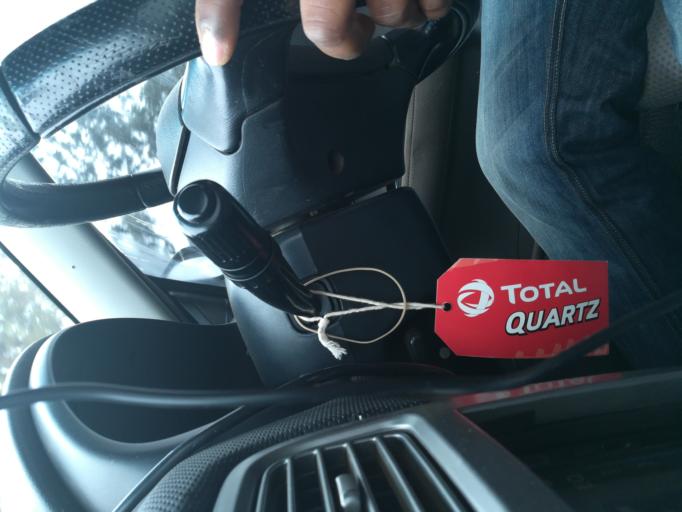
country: KE
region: Nairobi Area
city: Thika
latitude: -1.0422
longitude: 37.0708
